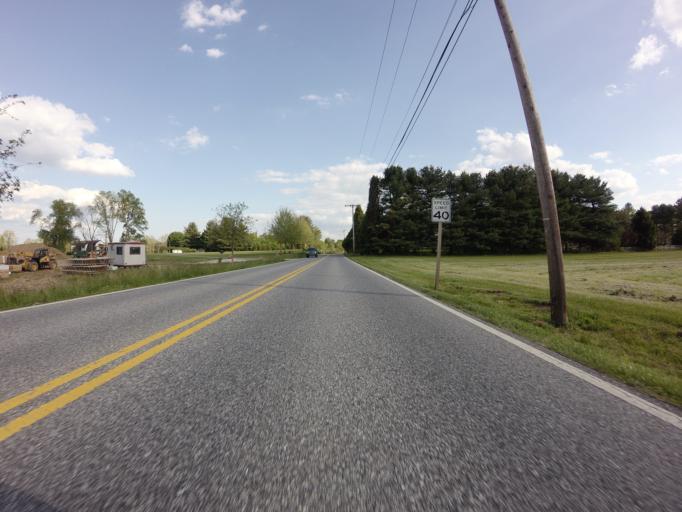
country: US
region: Maryland
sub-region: Baltimore County
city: Hunt Valley
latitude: 39.5317
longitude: -76.7261
